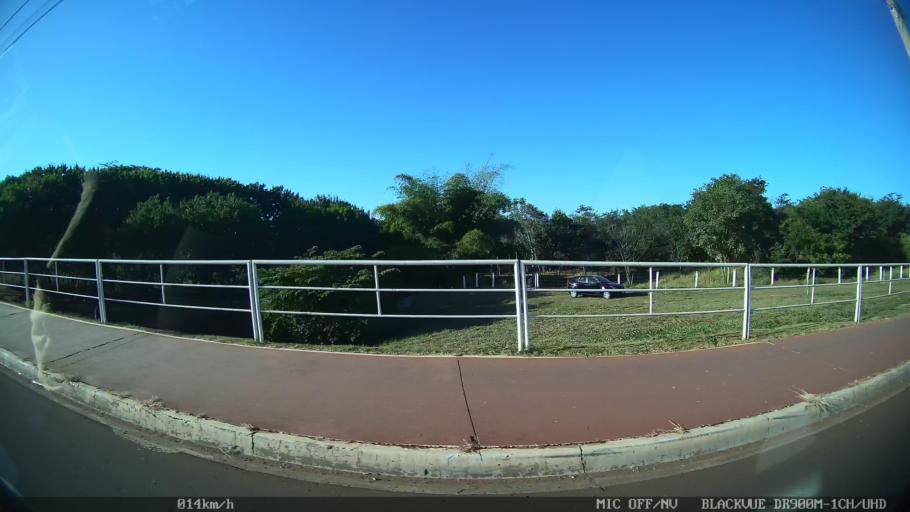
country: BR
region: Sao Paulo
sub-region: Guapiacu
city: Guapiacu
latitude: -20.7945
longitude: -49.2305
